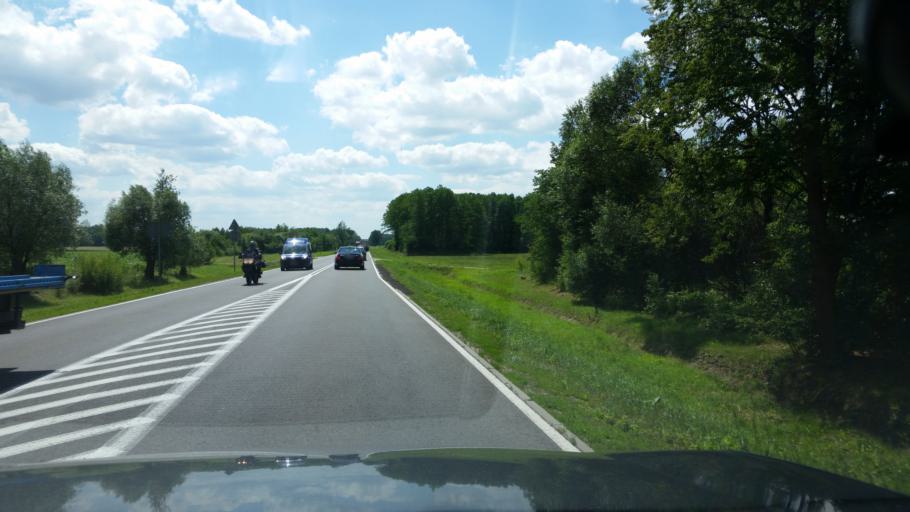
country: PL
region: Masovian Voivodeship
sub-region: Powiat ostrowski
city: Ostrow Mazowiecka
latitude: 52.9121
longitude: 21.8748
